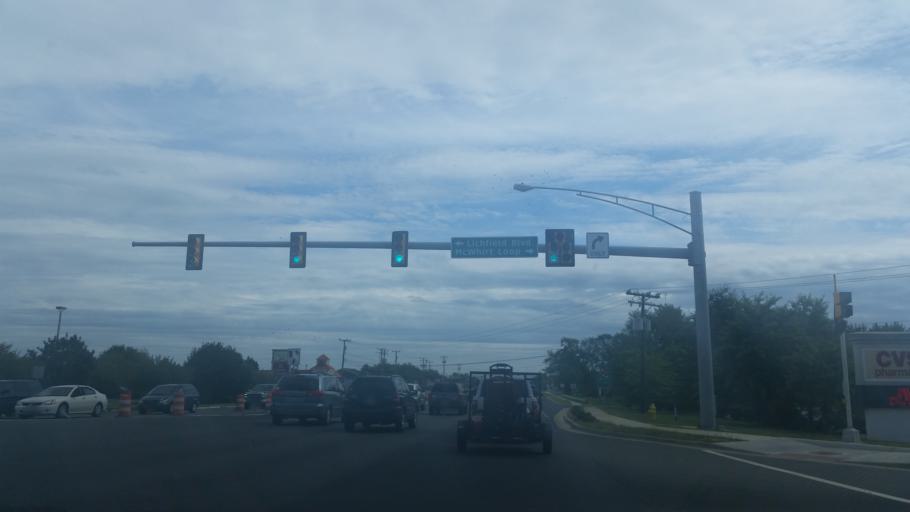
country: US
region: Virginia
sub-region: Stafford County
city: Falmouth
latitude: 38.3545
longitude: -77.5104
